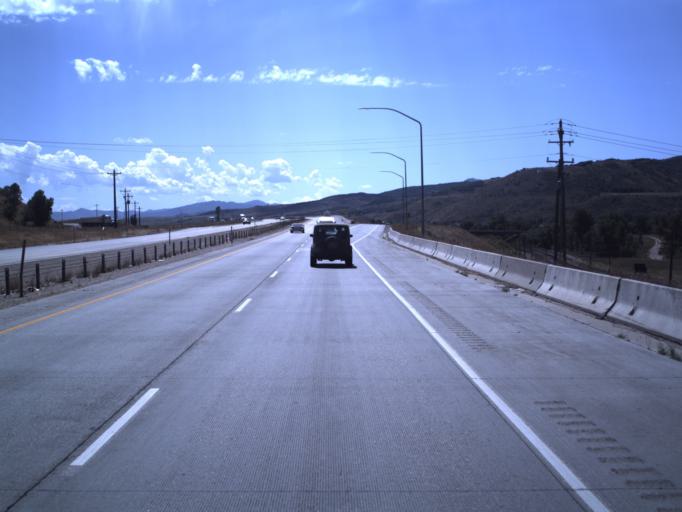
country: US
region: Utah
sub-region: Morgan County
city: Mountain Green
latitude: 41.1201
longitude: -111.7647
